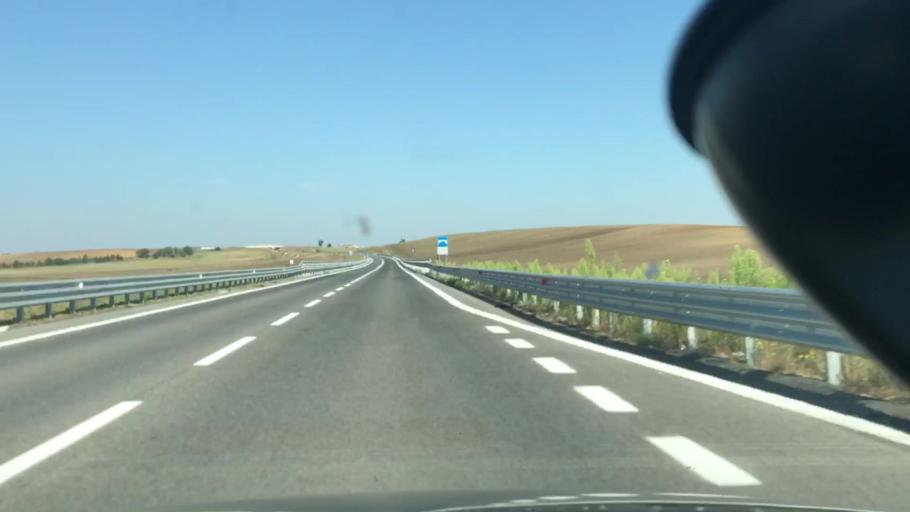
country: IT
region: Basilicate
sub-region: Provincia di Potenza
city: Palazzo San Gervasio
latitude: 40.9611
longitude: 16.0129
